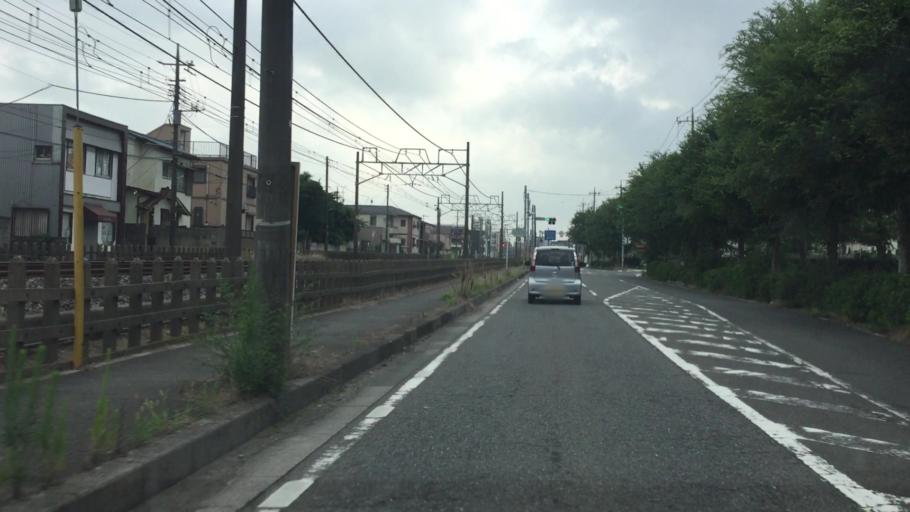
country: JP
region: Chiba
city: Matsudo
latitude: 35.8001
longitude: 139.9430
